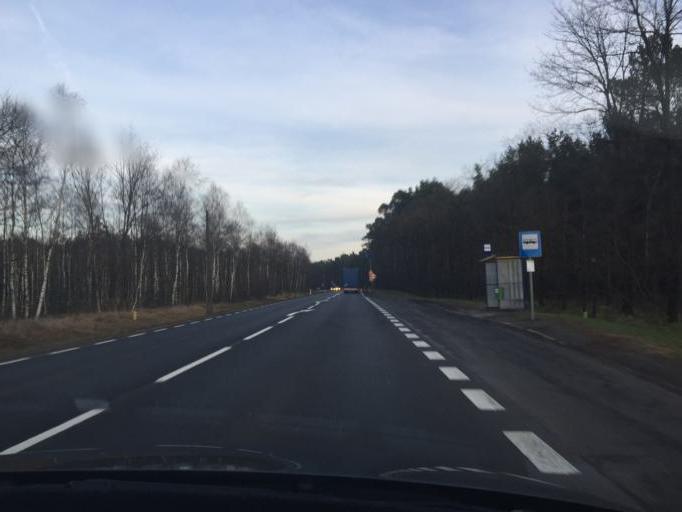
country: PL
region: Lubusz
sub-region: Powiat zielonogorski
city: Nowogrod Bobrzanski
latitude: 51.8156
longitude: 15.2838
